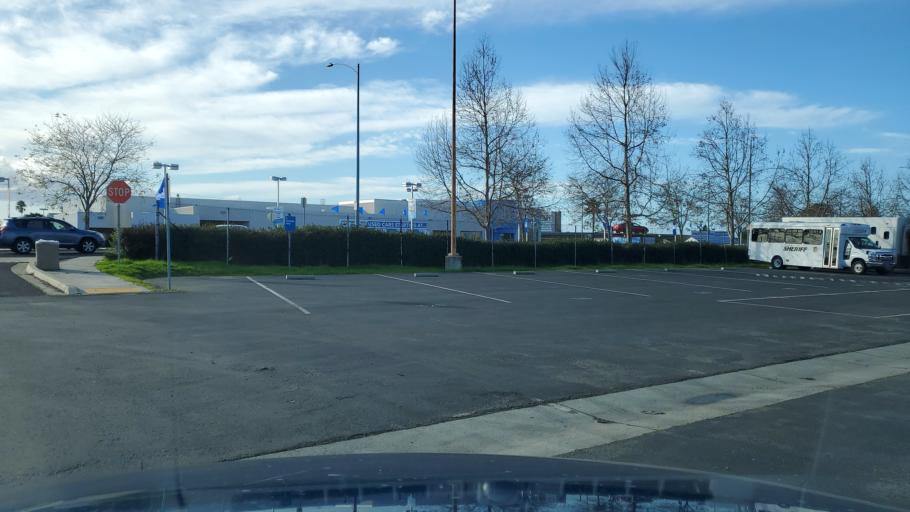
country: US
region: California
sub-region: Santa Clara County
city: Milpitas
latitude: 37.4188
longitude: -121.9113
